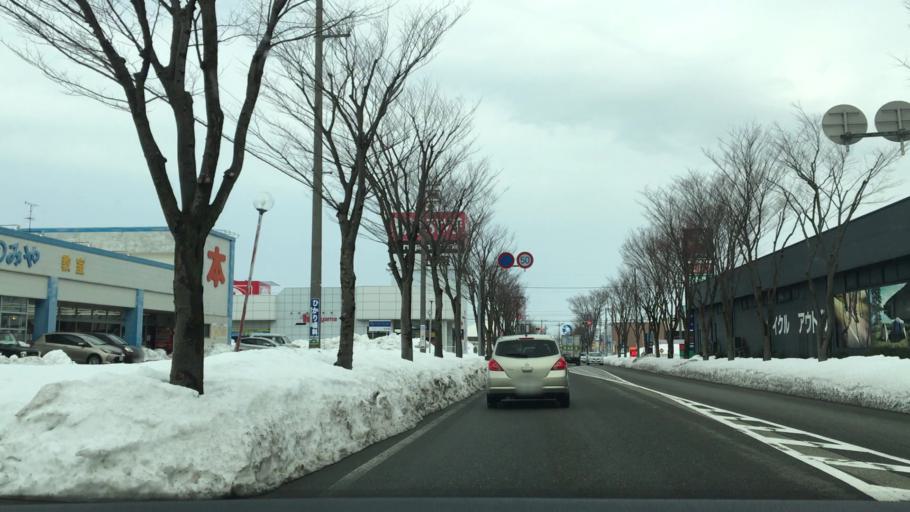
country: JP
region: Ishikawa
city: Nonoichi
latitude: 36.5048
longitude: 136.6070
